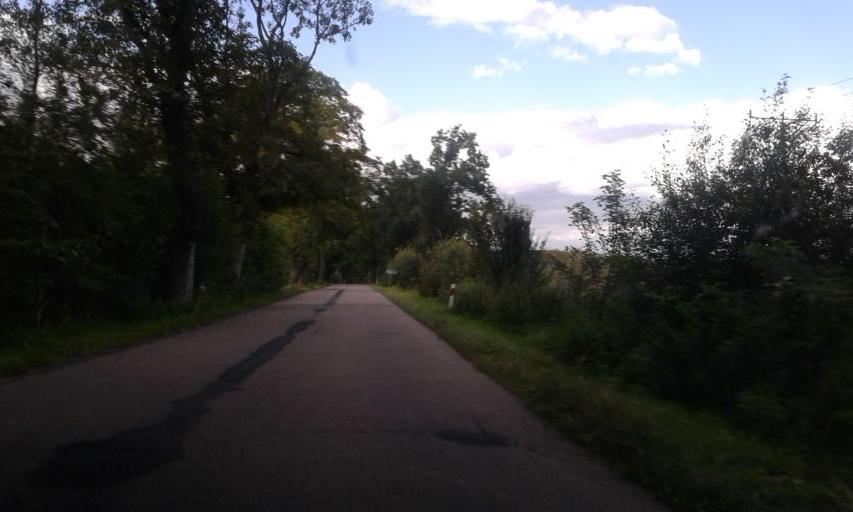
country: PL
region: West Pomeranian Voivodeship
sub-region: Powiat szczecinecki
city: Barwice
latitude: 53.7041
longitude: 16.3519
